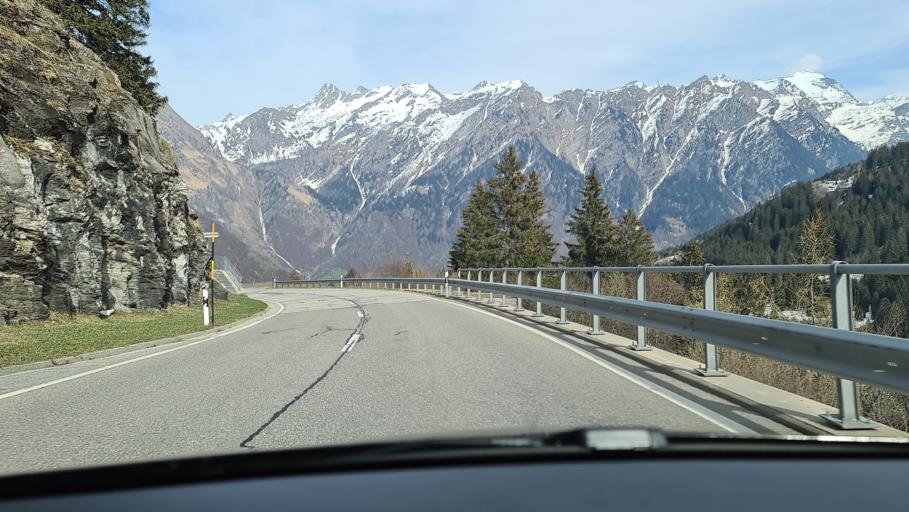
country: CH
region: Ticino
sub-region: Blenio District
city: Cancori
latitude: 46.5224
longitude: 8.8990
